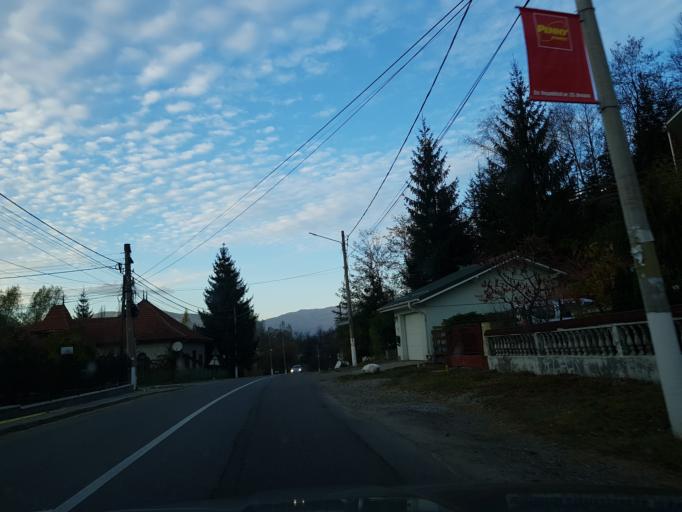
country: RO
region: Prahova
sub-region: Oras Breaza
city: Gura Beliei
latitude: 45.2131
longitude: 25.6448
